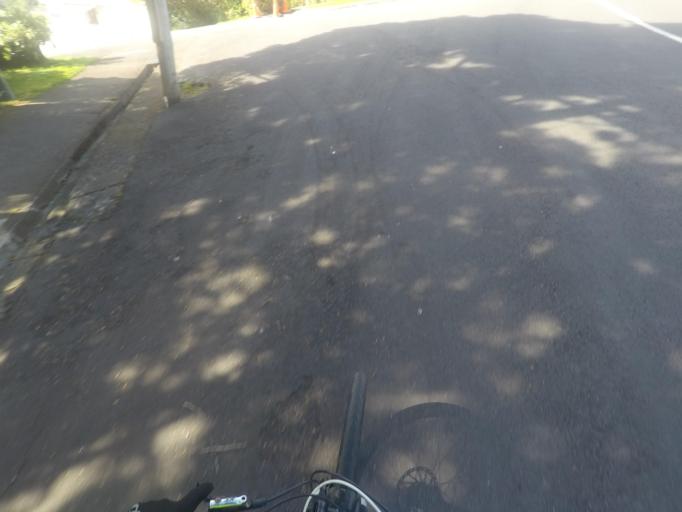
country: NZ
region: Auckland
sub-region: Auckland
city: Mangere
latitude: -36.9237
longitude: 174.7701
